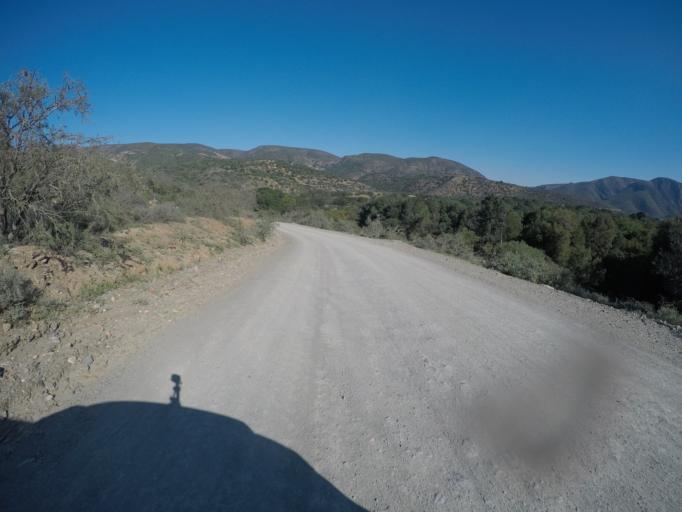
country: ZA
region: Eastern Cape
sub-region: Cacadu District Municipality
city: Kruisfontein
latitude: -33.6693
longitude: 24.5772
